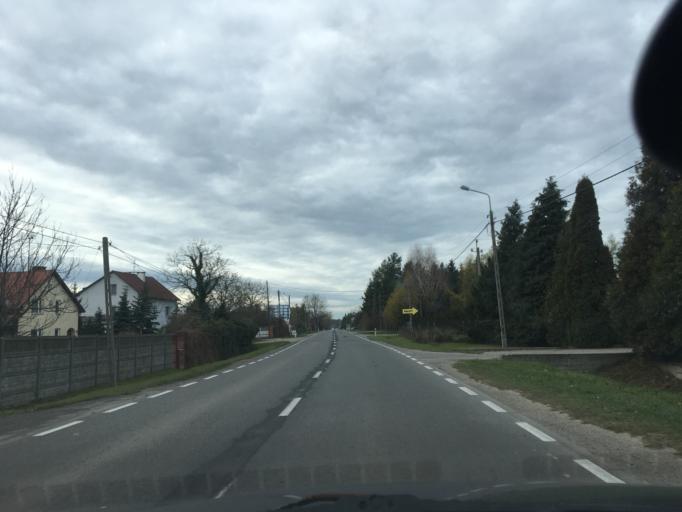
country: PL
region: Masovian Voivodeship
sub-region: Powiat piaseczynski
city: Tarczyn
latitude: 51.9790
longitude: 20.8519
